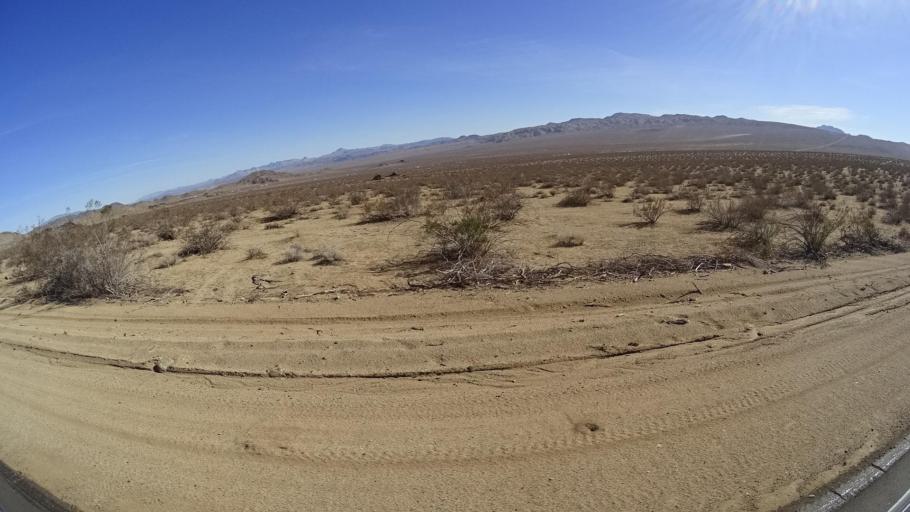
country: US
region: California
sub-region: Kern County
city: Ridgecrest
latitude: 35.5365
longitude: -117.5874
